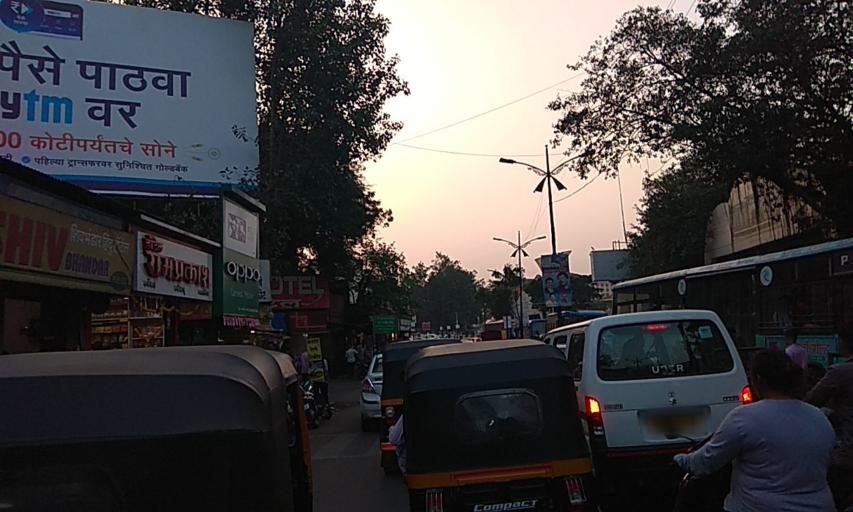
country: IN
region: Maharashtra
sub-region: Pune Division
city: Pune
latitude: 18.5280
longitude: 73.8750
